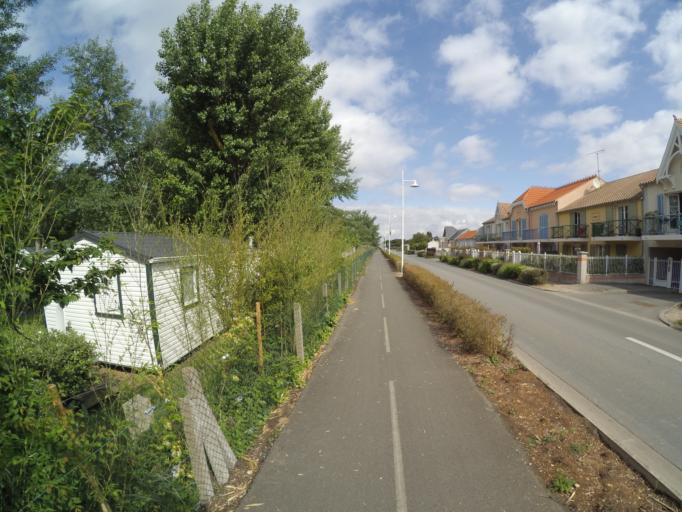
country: FR
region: Poitou-Charentes
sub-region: Departement de la Charente-Maritime
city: Chatelaillon-Plage
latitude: 46.0848
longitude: -1.0937
